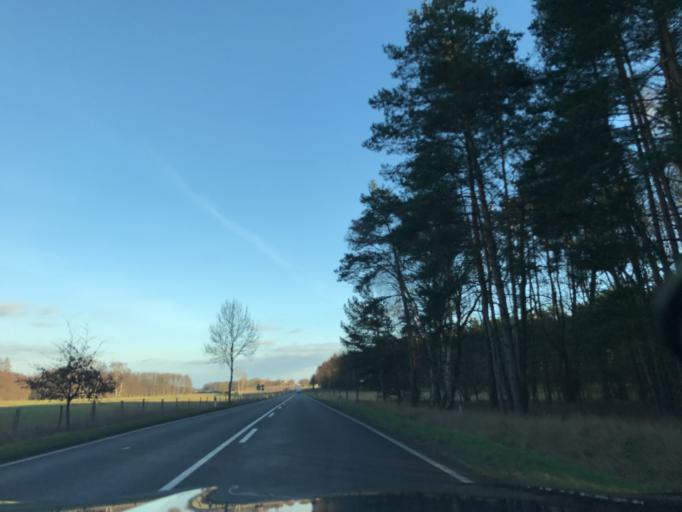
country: DE
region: Saxony-Anhalt
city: Burg bei Magdeburg
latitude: 52.2789
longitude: 11.9087
